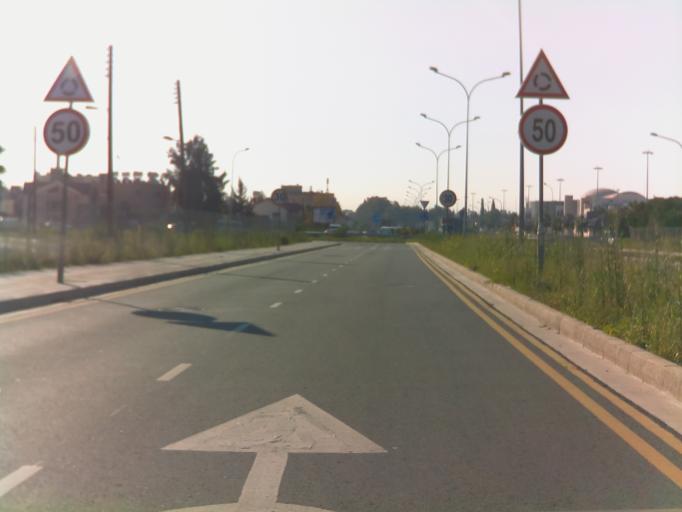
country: CY
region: Limassol
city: Ypsonas
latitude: 34.6580
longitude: 32.9967
